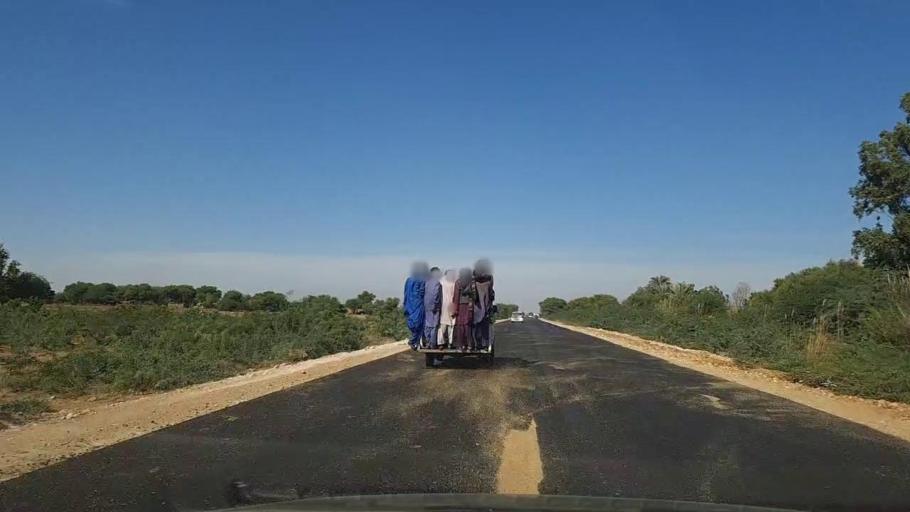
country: PK
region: Sindh
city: Kotri
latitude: 25.2322
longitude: 68.2342
